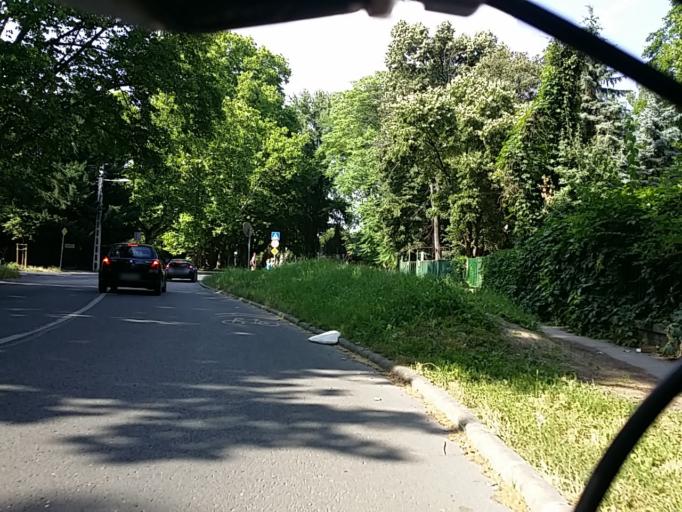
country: HU
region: Budapest
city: Budapest IV. keruelet
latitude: 47.5749
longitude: 19.0627
